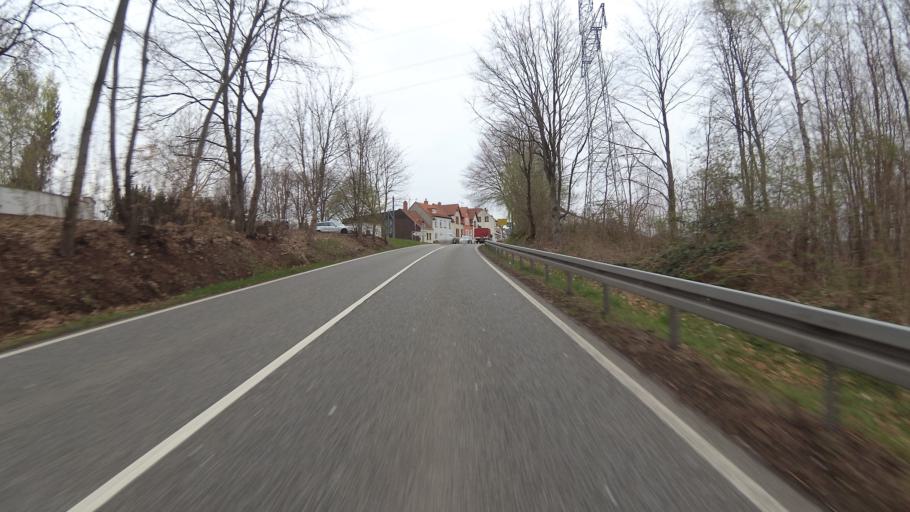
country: DE
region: Saarland
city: Spiesen-Elversberg
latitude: 49.3083
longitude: 7.1235
